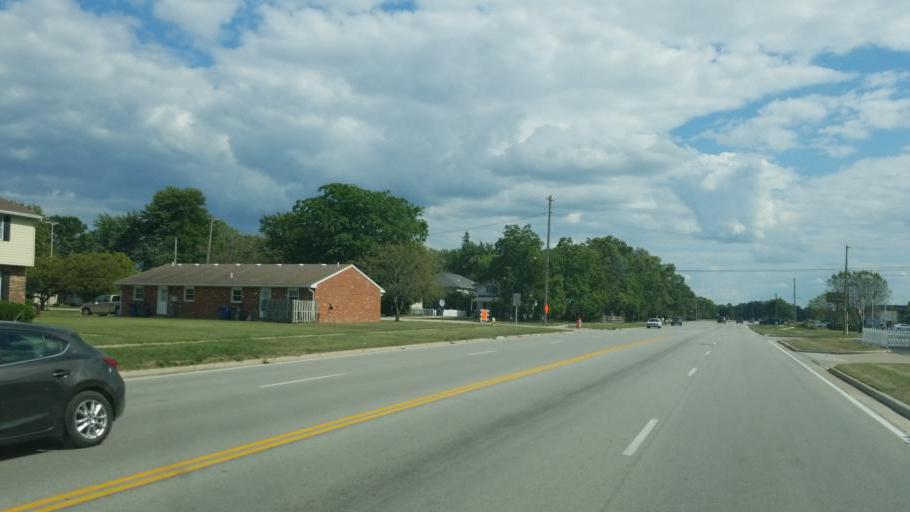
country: US
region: Ohio
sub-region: Wood County
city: Perrysburg
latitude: 41.5489
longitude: -83.6371
